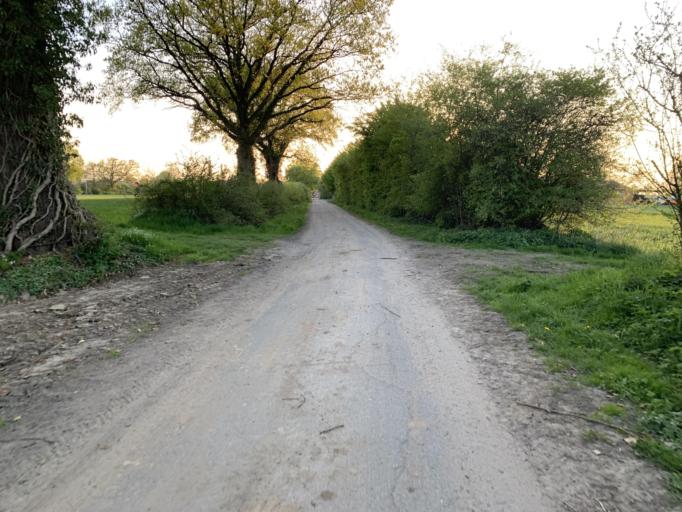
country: DE
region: Schleswig-Holstein
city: Worth
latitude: 53.4691
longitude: 10.4175
